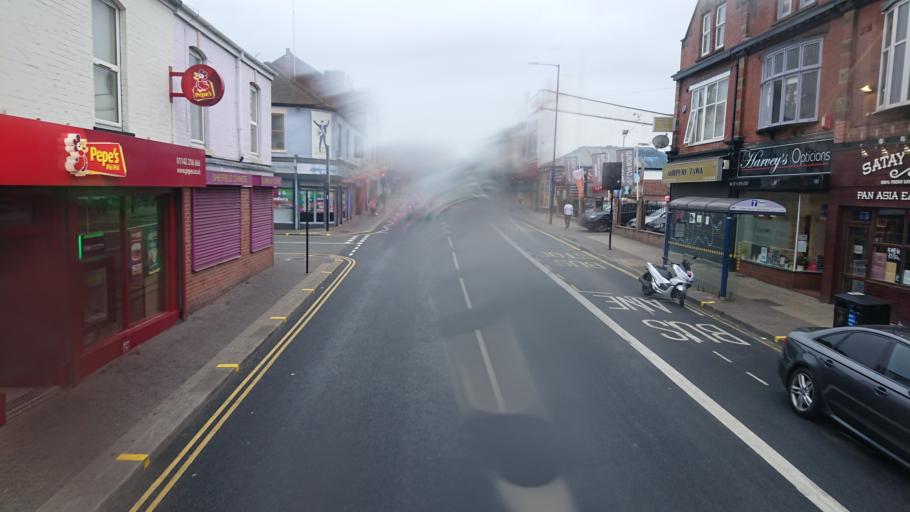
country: GB
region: England
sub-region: Sheffield
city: Sheffield
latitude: 53.3695
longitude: -1.4772
